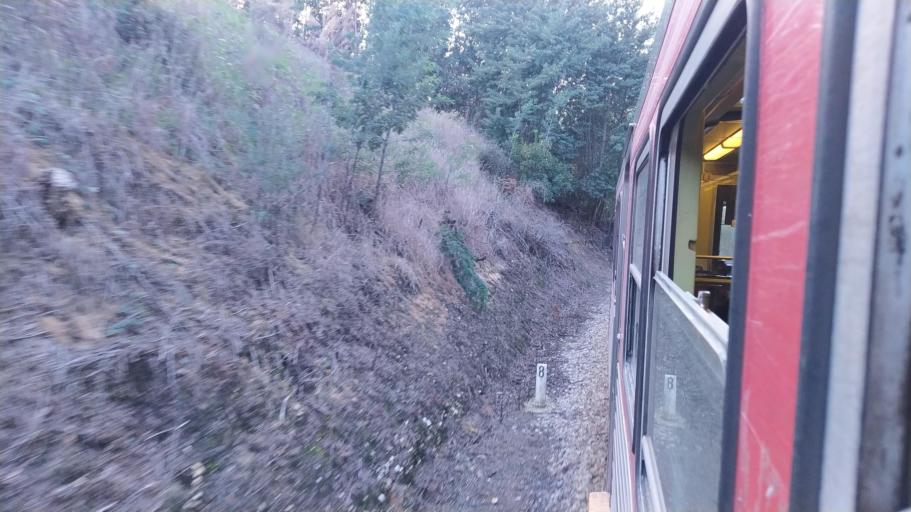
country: PT
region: Aveiro
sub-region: Aveiro
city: Eixo
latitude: 40.6348
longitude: -8.5781
